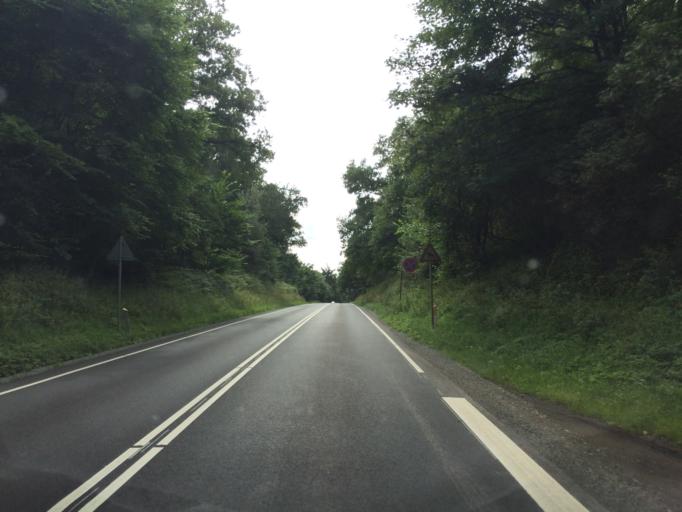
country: DK
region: South Denmark
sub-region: Faaborg-Midtfyn Kommune
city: Faaborg
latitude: 55.1288
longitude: 10.2572
